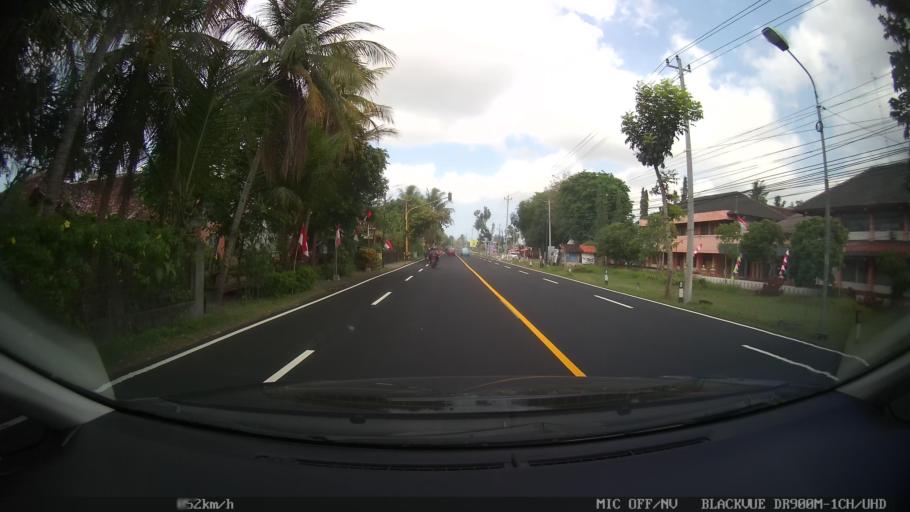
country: ID
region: Daerah Istimewa Yogyakarta
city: Srandakan
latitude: -7.8714
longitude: 110.1407
